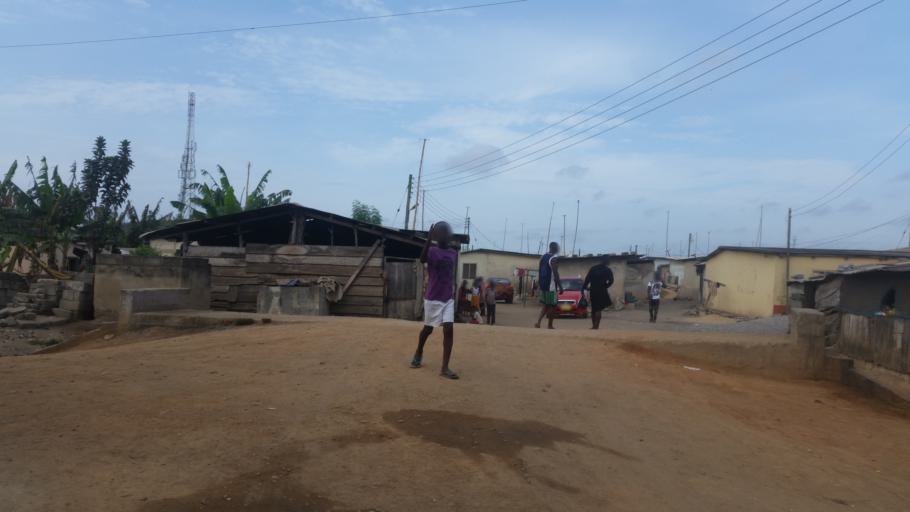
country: GH
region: Central
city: Cape Coast
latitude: 5.1238
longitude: -1.3011
